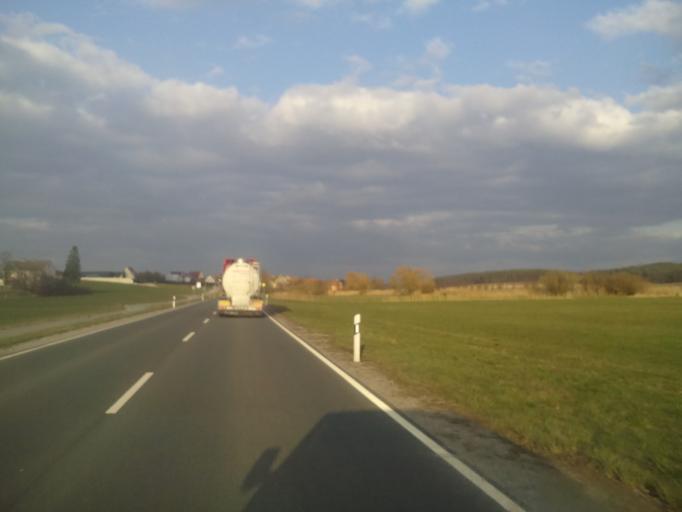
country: DE
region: Bavaria
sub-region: Regierungsbezirk Mittelfranken
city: Uehlfeld
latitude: 49.6786
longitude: 10.7398
